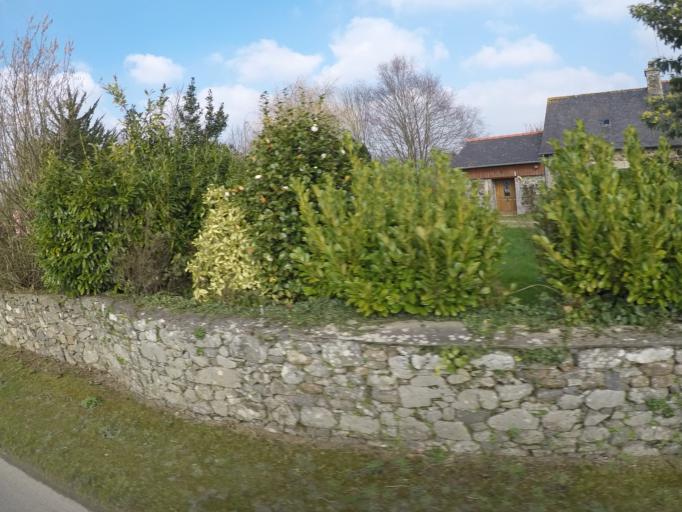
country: FR
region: Brittany
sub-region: Departement des Cotes-d'Armor
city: Pommerit-le-Vicomte
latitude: 48.6188
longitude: -3.0789
